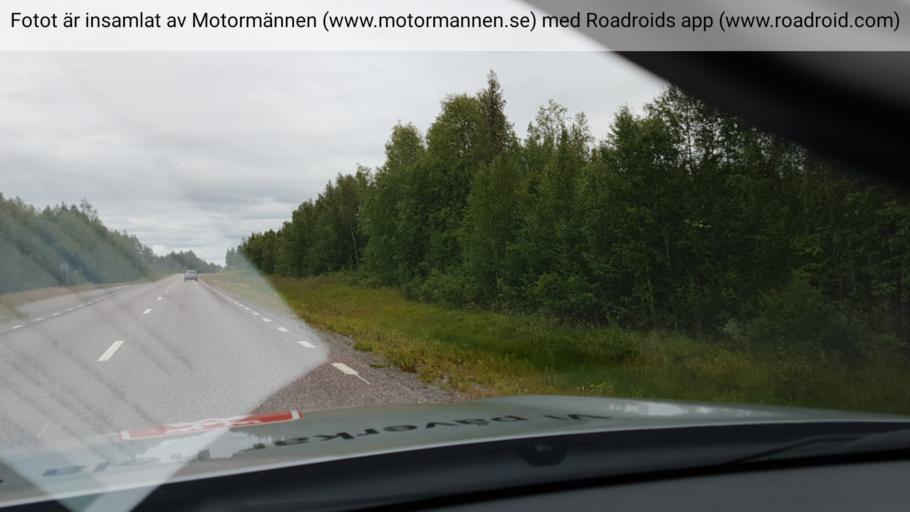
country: SE
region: Norrbotten
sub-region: Gallivare Kommun
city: Gaellivare
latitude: 67.0303
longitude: 21.7374
